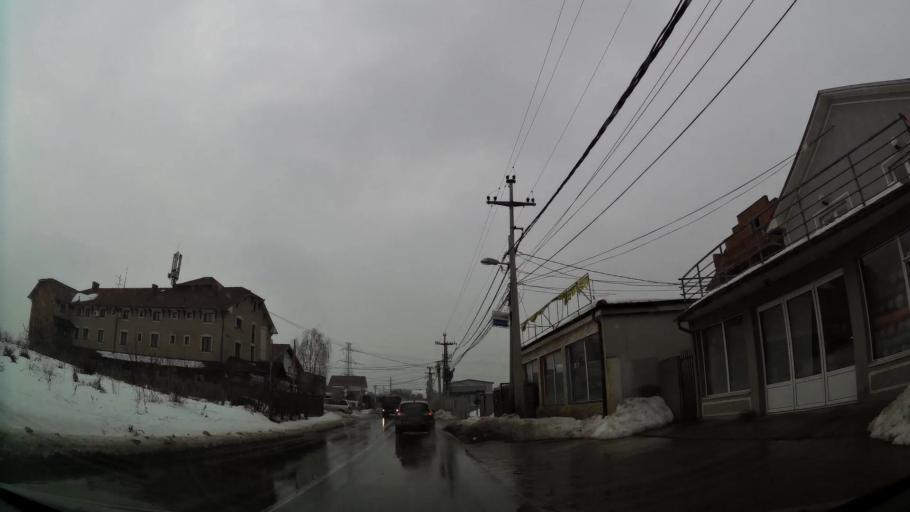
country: RS
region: Central Serbia
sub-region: Belgrade
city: Zvezdara
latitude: 44.7662
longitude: 20.5333
